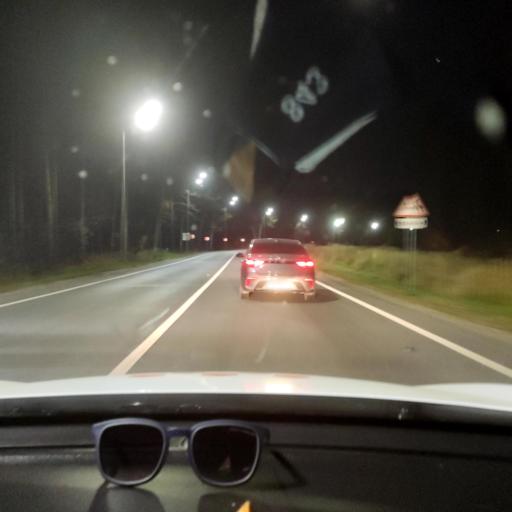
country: RU
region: Tatarstan
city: Stolbishchi
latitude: 55.6341
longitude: 49.1032
